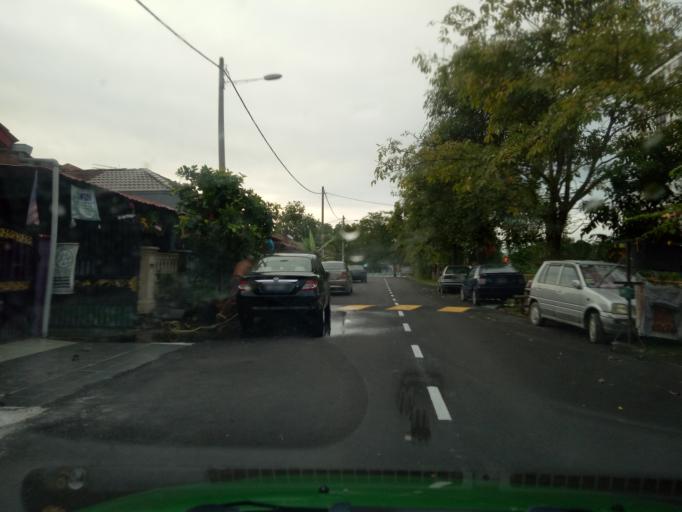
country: MY
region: Selangor
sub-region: Hulu Langat
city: Semenyih
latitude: 2.9269
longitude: 101.8608
